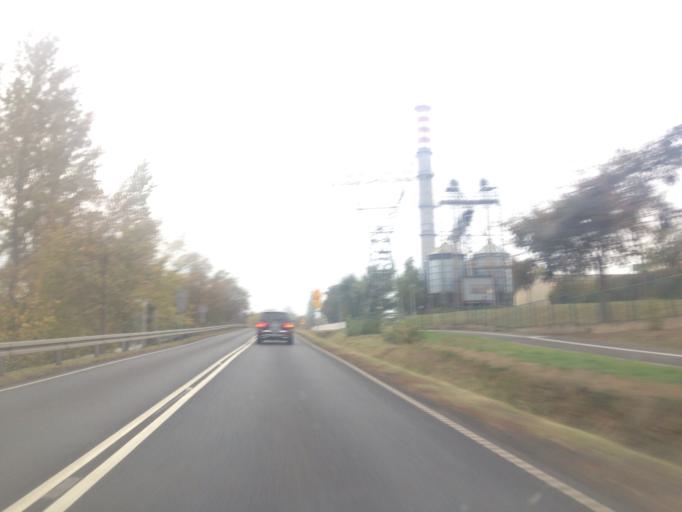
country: PL
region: Greater Poland Voivodeship
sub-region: Powiat gnieznienski
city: Trzemeszno
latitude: 52.5652
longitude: 17.8197
